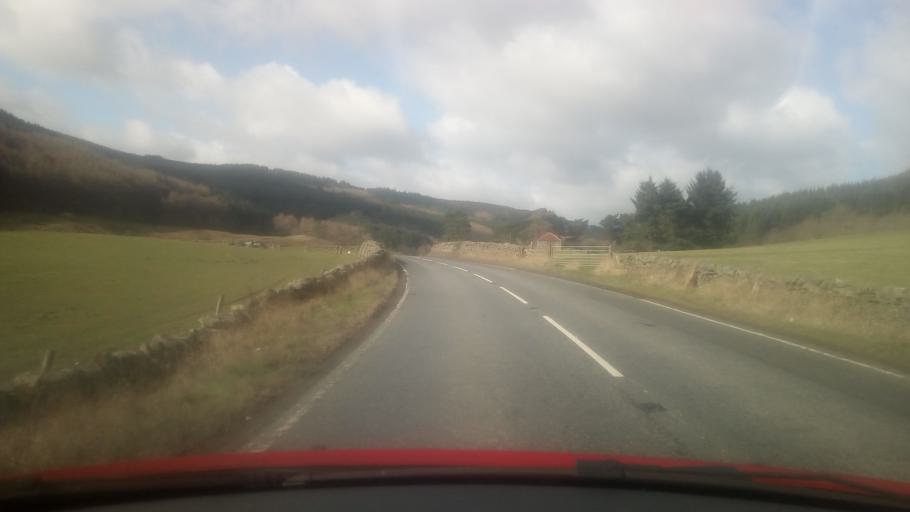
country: GB
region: Scotland
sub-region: The Scottish Borders
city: Selkirk
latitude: 55.6165
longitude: -2.9402
